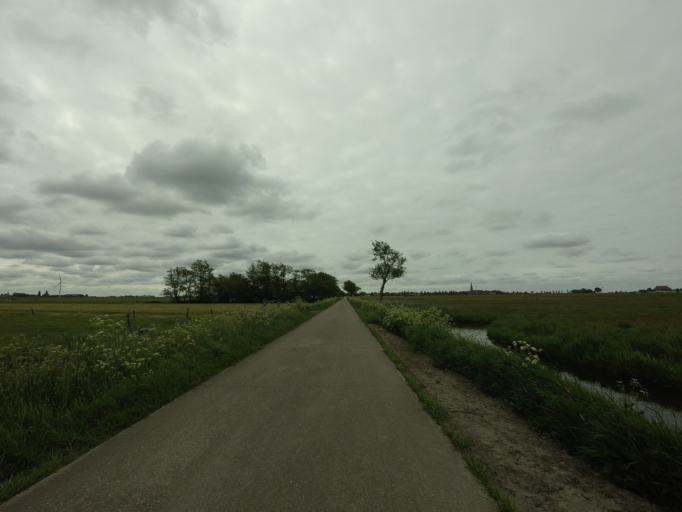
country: NL
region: Friesland
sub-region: Sudwest Fryslan
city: Workum
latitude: 52.9928
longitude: 5.4585
